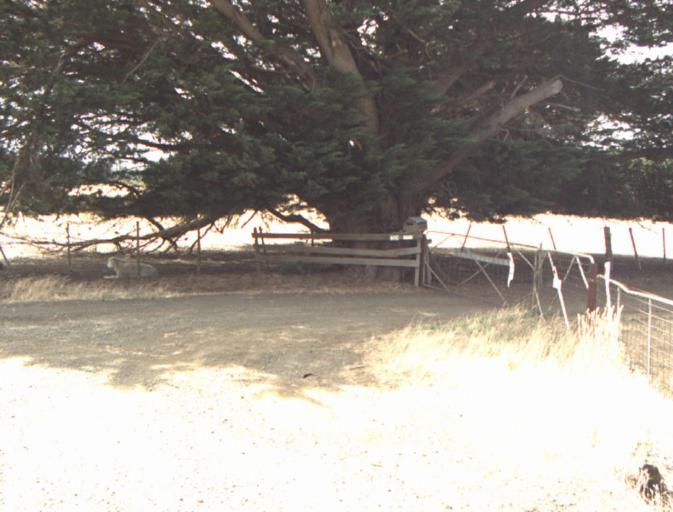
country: AU
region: Tasmania
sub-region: Northern Midlands
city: Evandale
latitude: -41.5232
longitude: 147.2841
